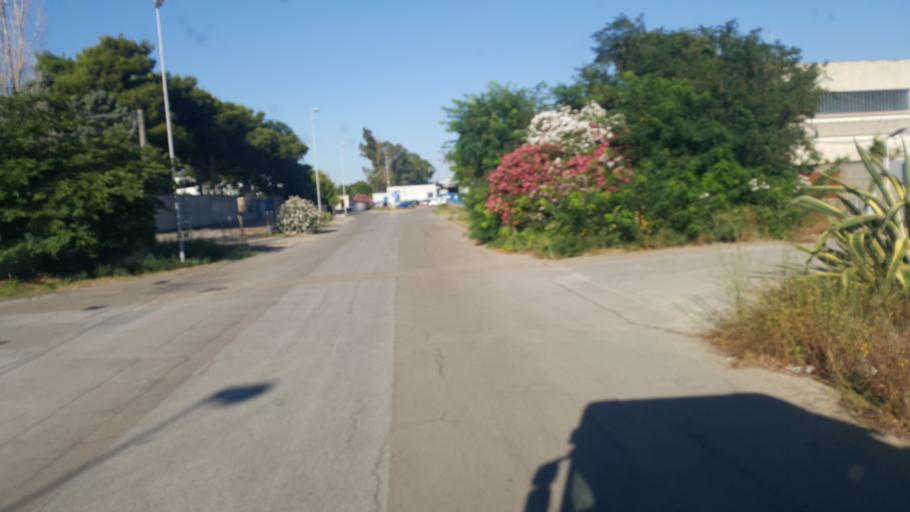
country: IT
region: Apulia
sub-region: Provincia di Brindisi
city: Materdomini
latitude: 40.6319
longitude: 17.9761
